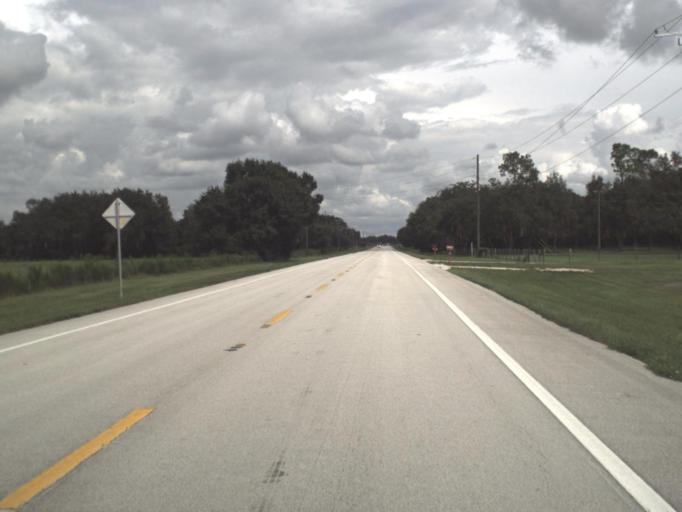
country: US
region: Florida
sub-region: DeSoto County
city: Nocatee
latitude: 27.2006
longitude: -81.9762
